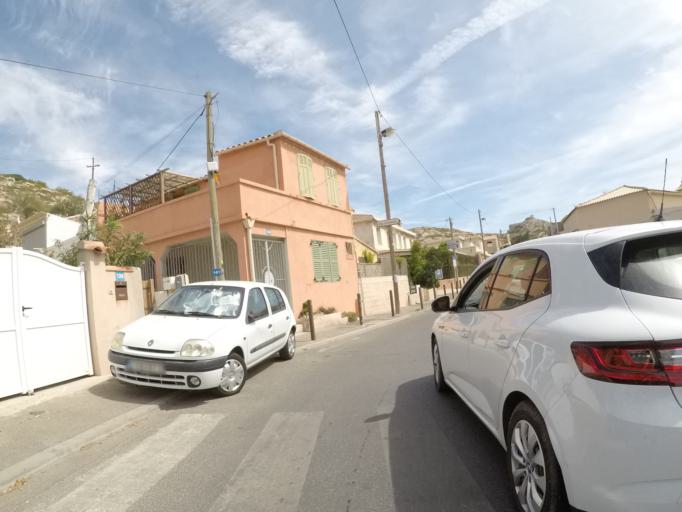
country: FR
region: Provence-Alpes-Cote d'Azur
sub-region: Departement des Bouches-du-Rhone
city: Marseille 08
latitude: 43.2155
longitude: 5.3474
